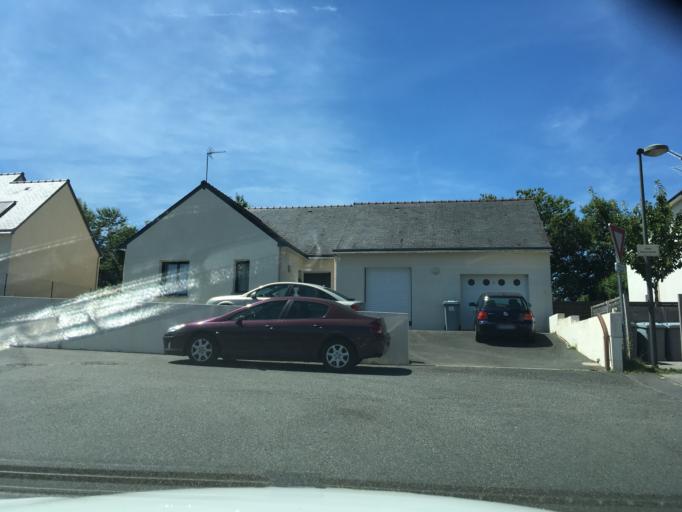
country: FR
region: Brittany
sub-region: Departement du Finistere
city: Quimper
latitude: 48.0046
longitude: -4.1275
